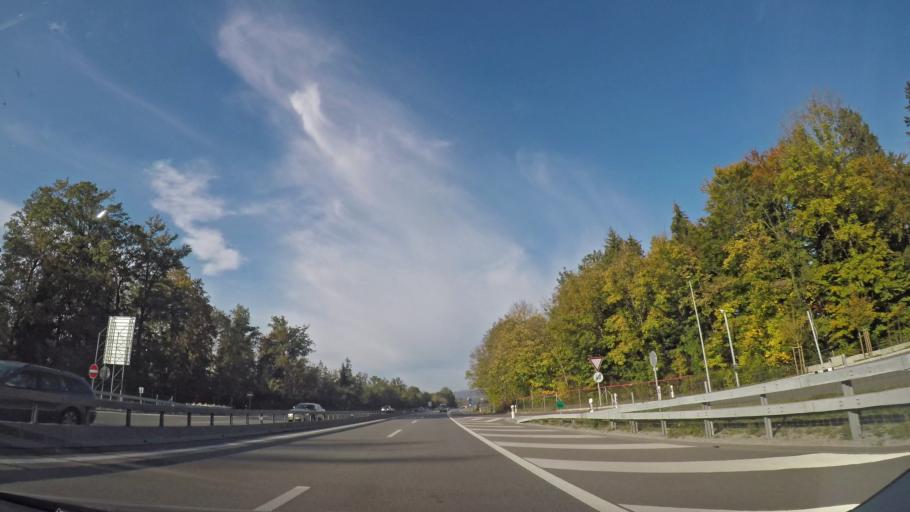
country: CH
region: Bern
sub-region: Bern-Mittelland District
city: Rubigen
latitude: 46.8792
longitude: 7.5419
